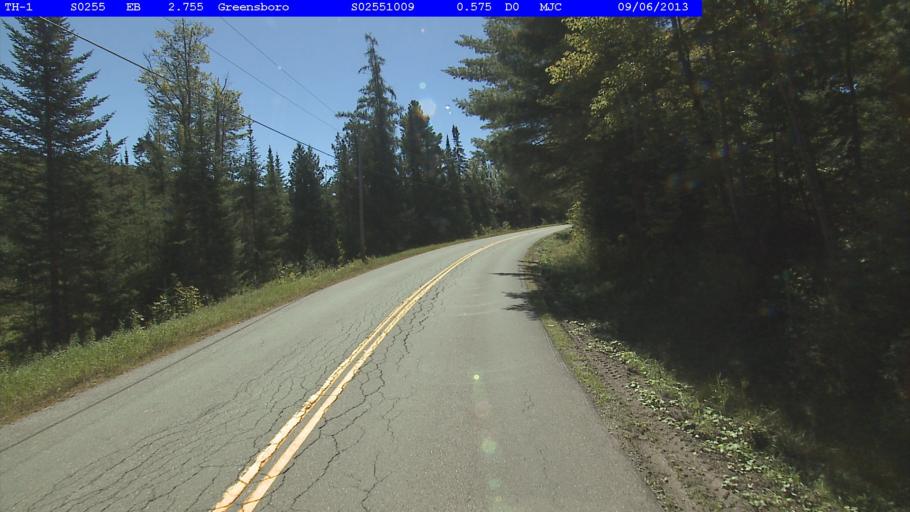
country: US
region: Vermont
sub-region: Caledonia County
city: Hardwick
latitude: 44.6325
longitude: -72.3270
